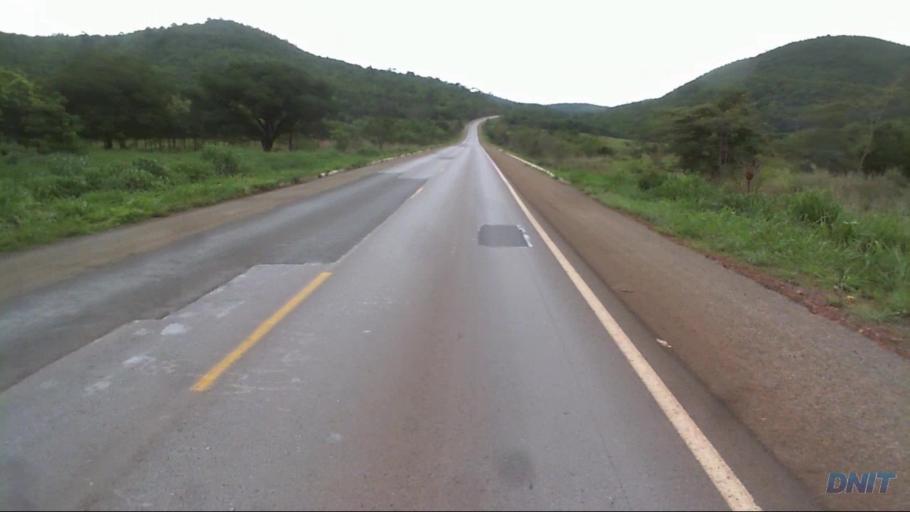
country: BR
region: Goias
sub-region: Barro Alto
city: Barro Alto
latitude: -14.9108
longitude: -48.9571
